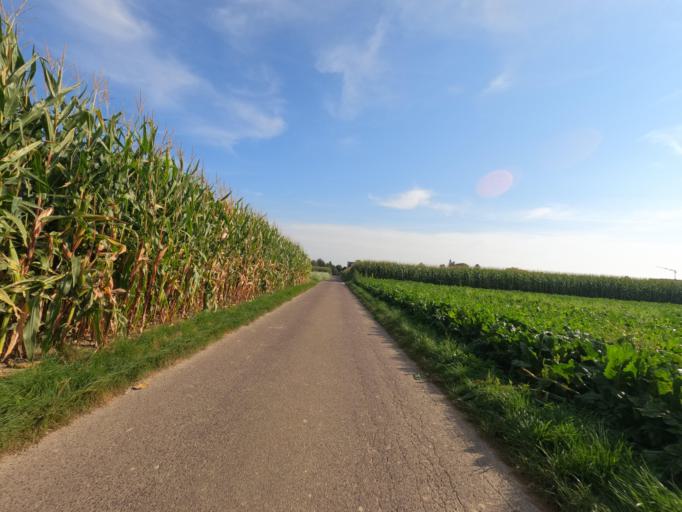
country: DE
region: North Rhine-Westphalia
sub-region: Regierungsbezirk Koln
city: Linnich
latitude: 51.0037
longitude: 6.2289
